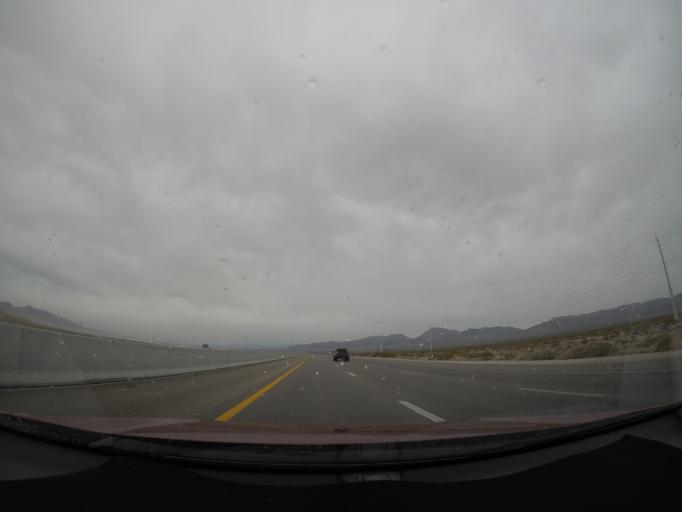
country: US
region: Nevada
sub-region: Clark County
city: Enterprise
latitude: 35.7666
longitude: -115.3388
